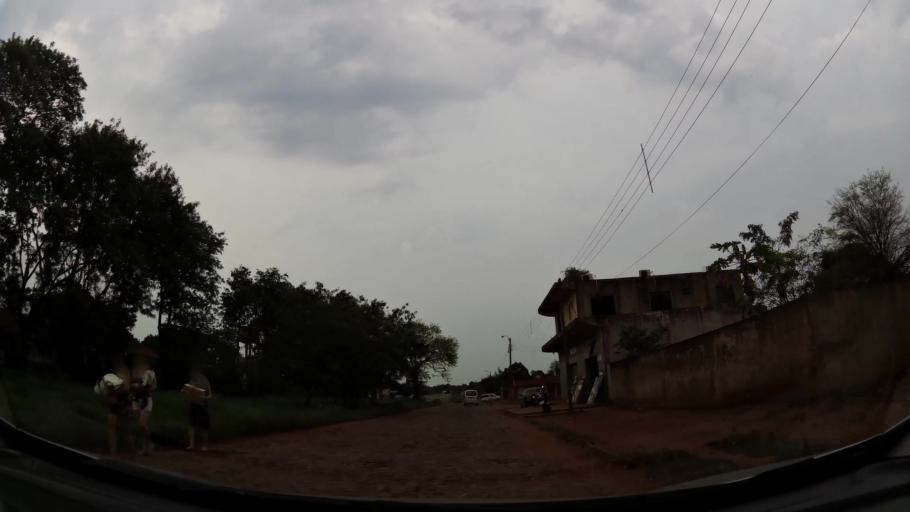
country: PY
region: Alto Parana
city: Presidente Franco
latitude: -25.5408
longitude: -54.6516
